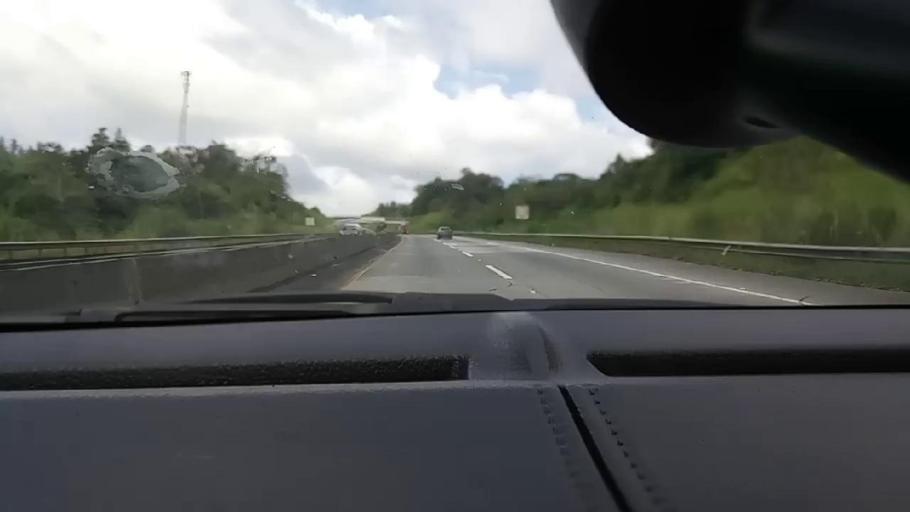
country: PA
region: Colon
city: Gatun
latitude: 9.2913
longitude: -79.7813
